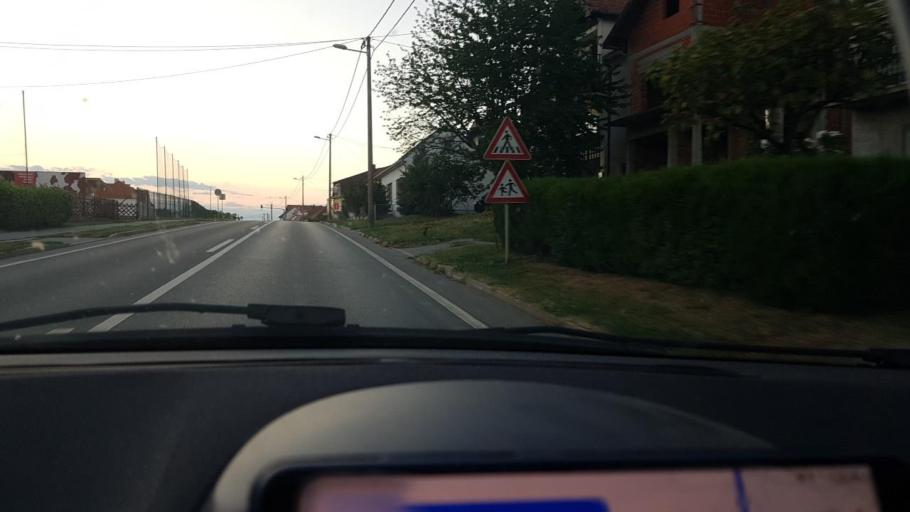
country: HR
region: Bjelovarsko-Bilogorska
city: Zdralovi
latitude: 45.8822
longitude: 16.8673
